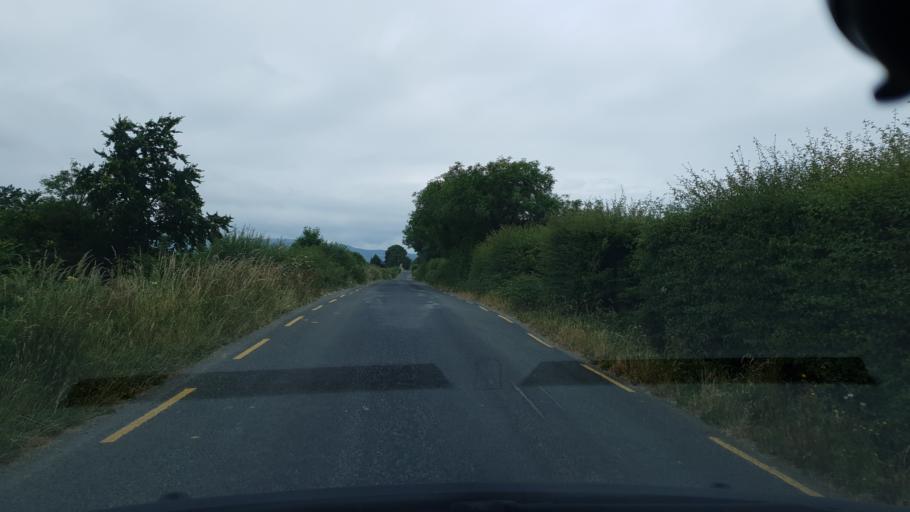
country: IE
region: Munster
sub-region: Ciarrai
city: Cill Airne
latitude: 52.1425
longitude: -9.5889
